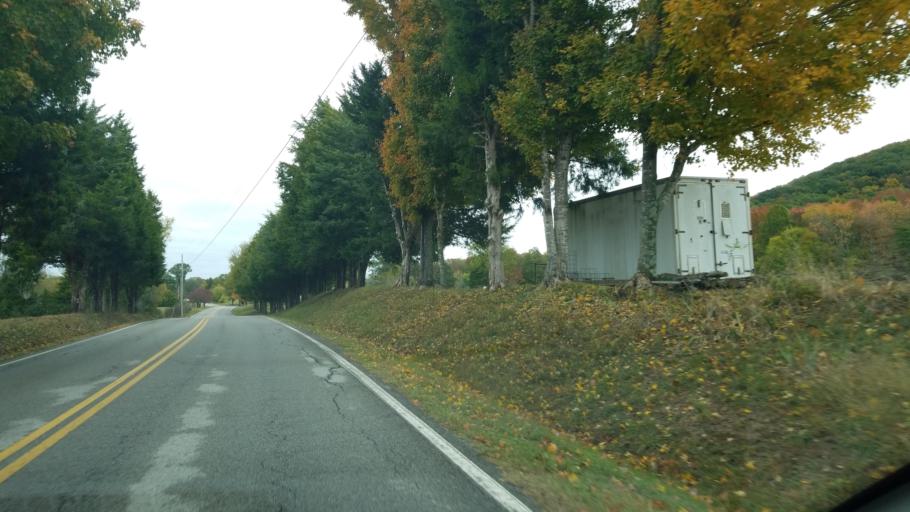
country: US
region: Tennessee
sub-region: Bradley County
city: Hopewell
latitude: 35.2594
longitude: -84.9752
